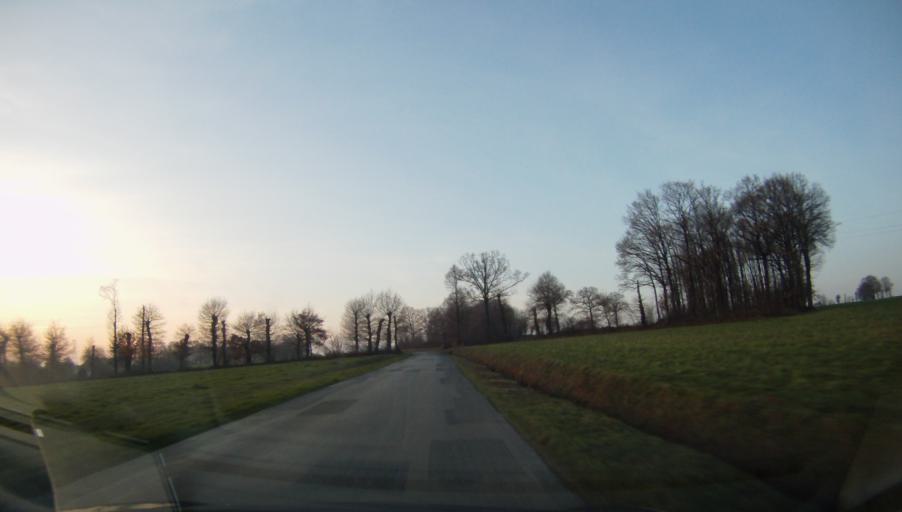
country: FR
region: Brittany
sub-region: Departement d'Ille-et-Vilaine
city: Chanteloup
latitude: 47.9283
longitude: -1.6270
